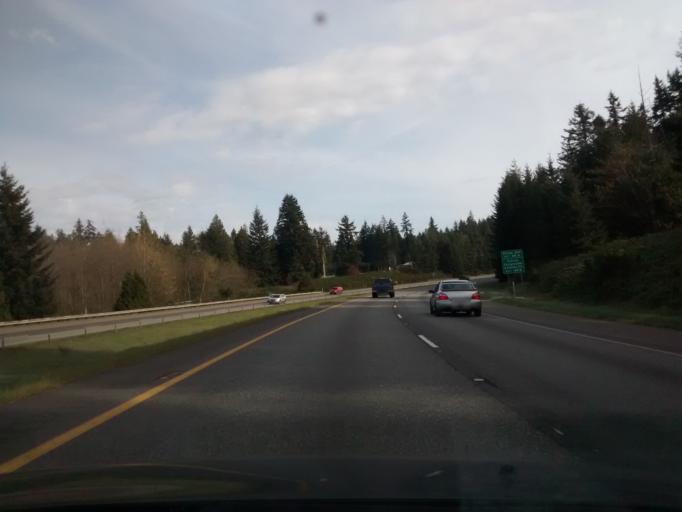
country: US
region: Washington
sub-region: Kitsap County
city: Silverdale
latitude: 47.6565
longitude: -122.7050
